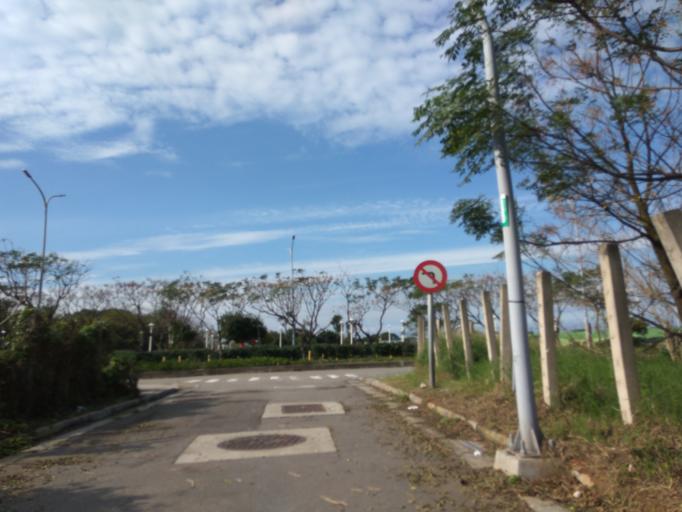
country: TW
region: Taiwan
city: Taoyuan City
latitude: 25.0525
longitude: 121.1755
